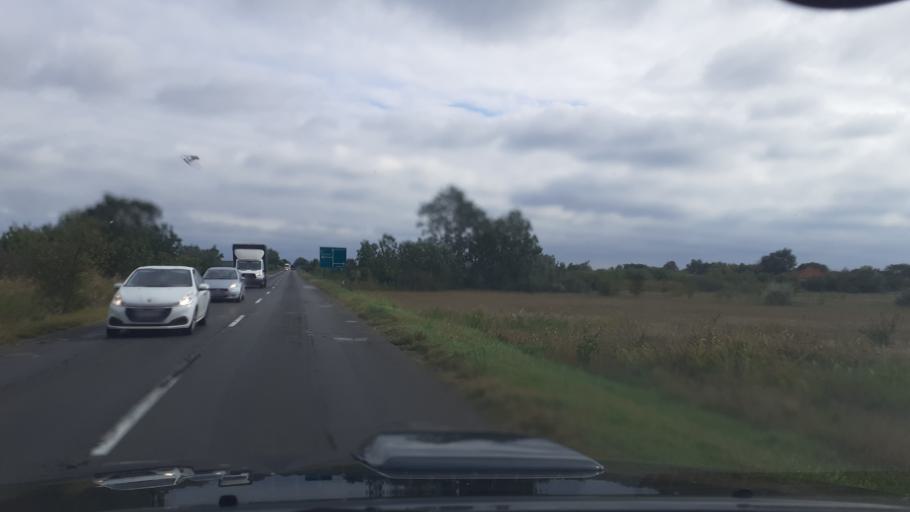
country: HU
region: Bacs-Kiskun
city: Fulopszallas
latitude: 46.8299
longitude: 19.2318
